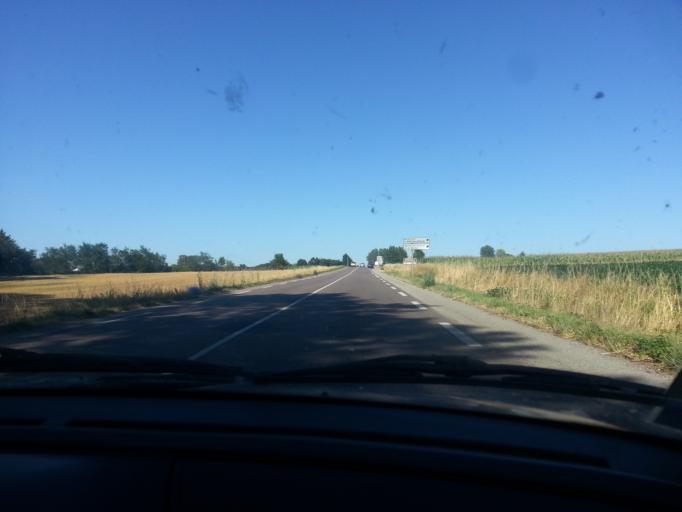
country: FR
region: Bourgogne
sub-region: Departement de Saone-et-Loire
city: Sassenay
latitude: 46.7976
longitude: 4.9308
